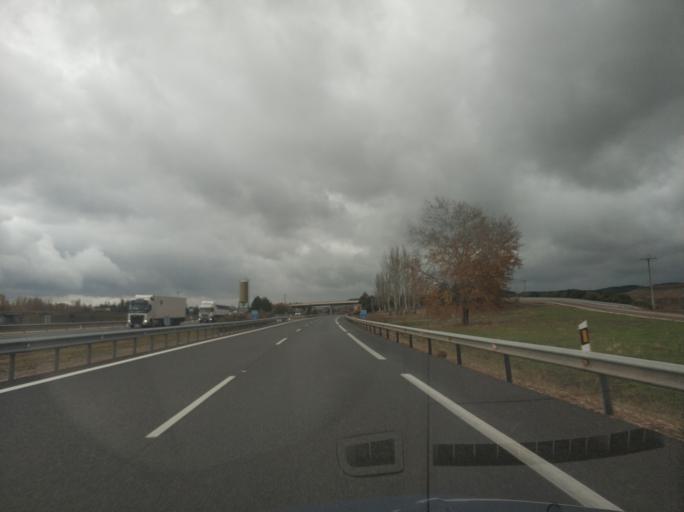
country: ES
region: Castille and Leon
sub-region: Provincia de Palencia
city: Reinoso de Cerrato
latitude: 41.9897
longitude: -4.4089
